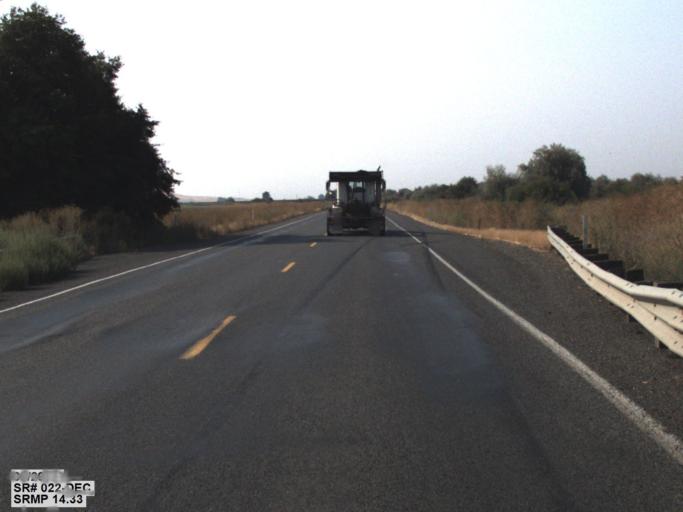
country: US
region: Washington
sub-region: Yakima County
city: Granger
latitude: 46.2744
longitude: -120.1561
